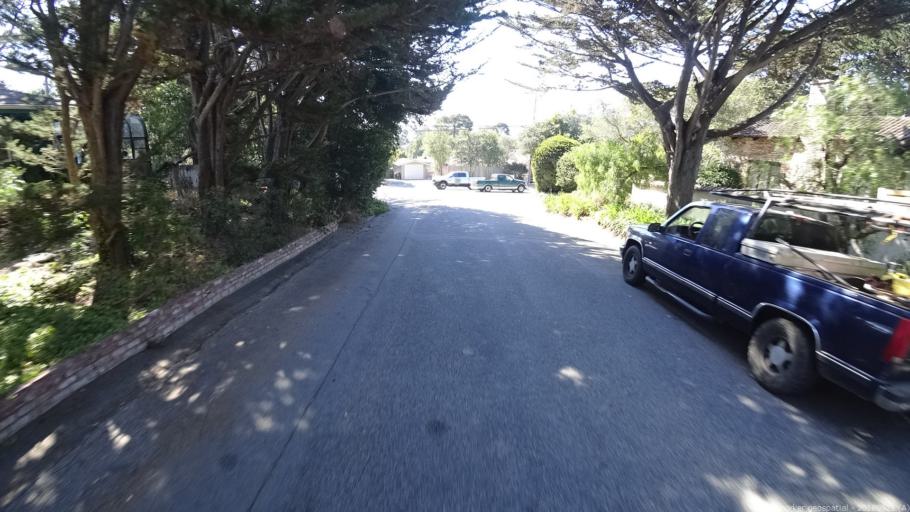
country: US
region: California
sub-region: Monterey County
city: Carmel-by-the-Sea
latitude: 36.5559
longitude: -121.9133
